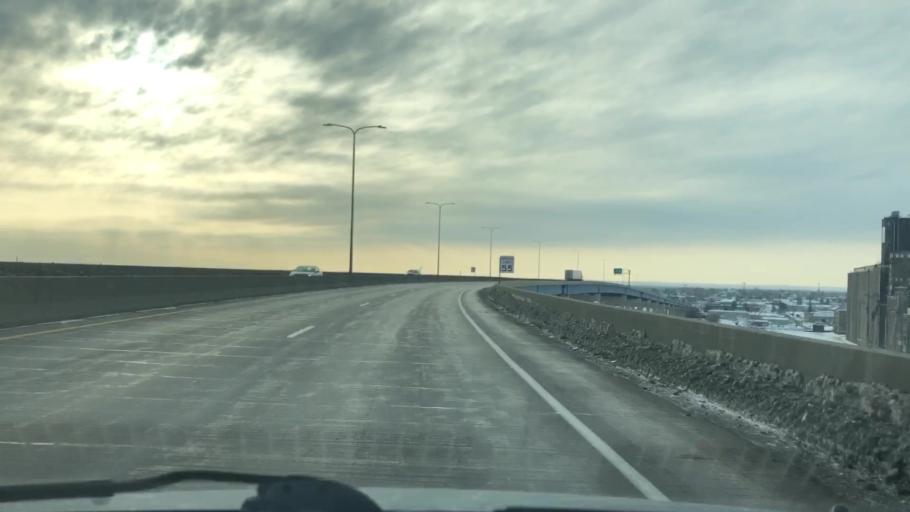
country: US
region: Wisconsin
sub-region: Douglas County
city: Superior
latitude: 46.7450
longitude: -92.0984
